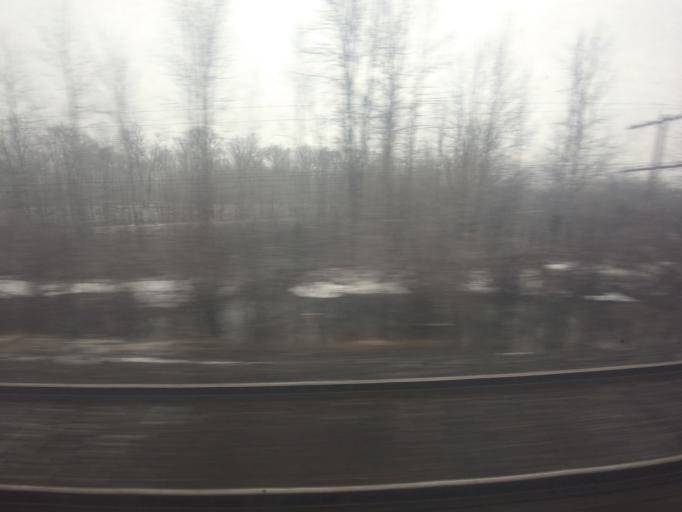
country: CA
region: Ontario
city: Brockville
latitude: 44.5715
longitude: -75.7557
